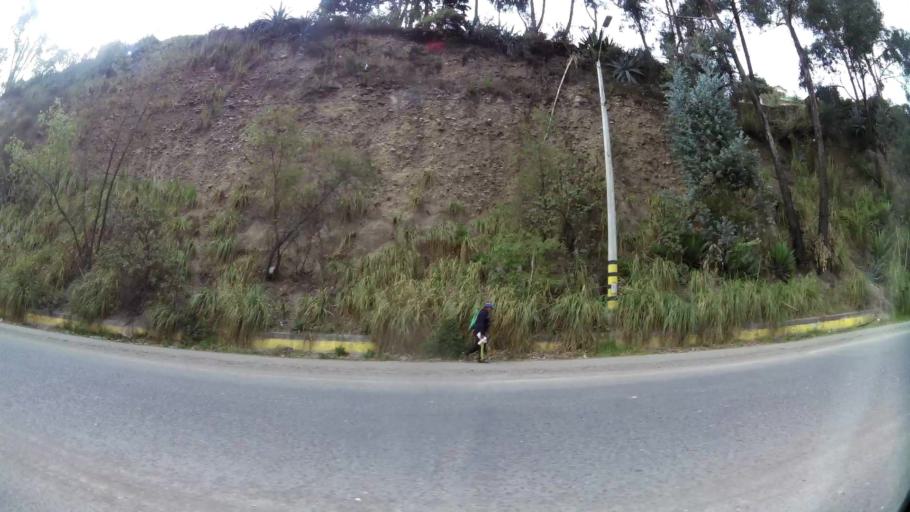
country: EC
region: Azuay
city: Cuenca
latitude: -2.8827
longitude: -78.9684
